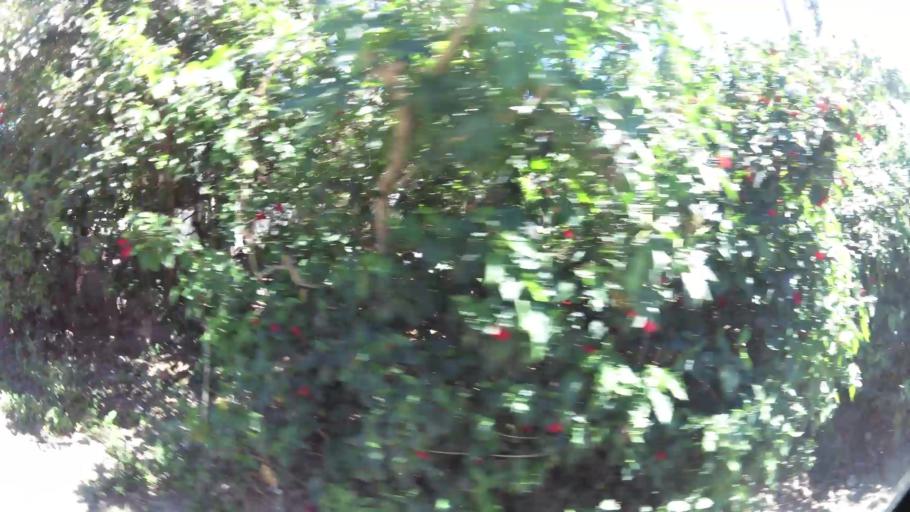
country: AR
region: Santa Fe
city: Santa Fe de la Vera Cruz
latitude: -31.6313
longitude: -60.7234
